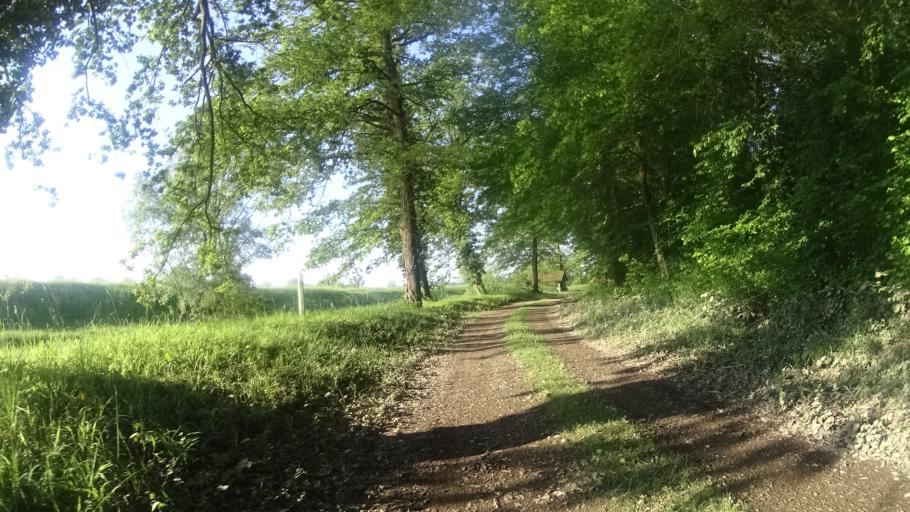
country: DE
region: Baden-Wuerttemberg
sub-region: Freiburg Region
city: Rheinau
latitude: 48.7022
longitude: 7.9580
